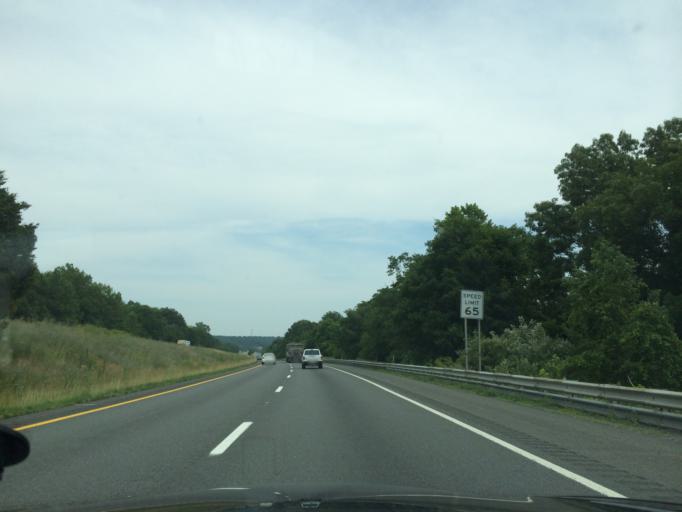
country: US
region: Maryland
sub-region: Washington County
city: Hancock
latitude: 39.6891
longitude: -78.1263
